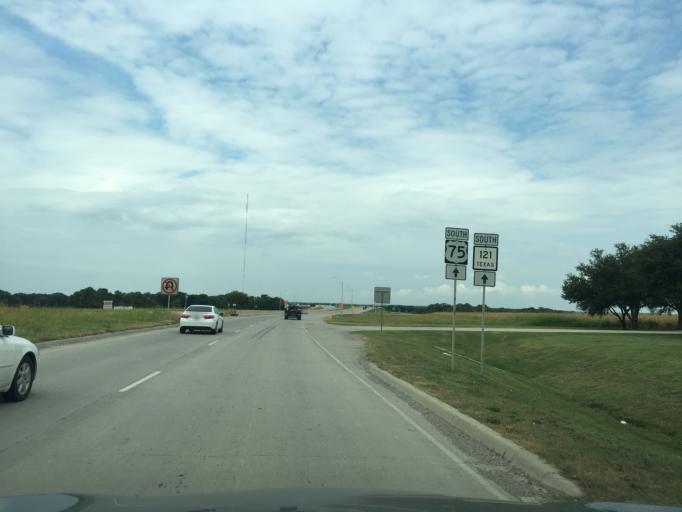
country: US
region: Texas
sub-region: Collin County
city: Melissa
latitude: 33.2654
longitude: -96.5917
